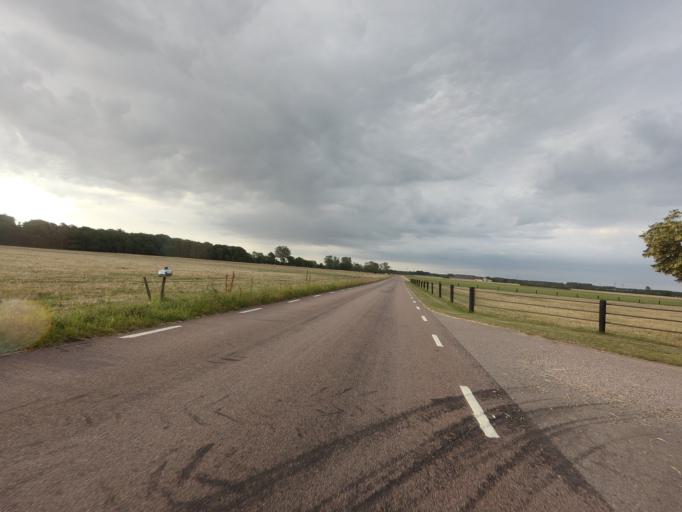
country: SE
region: Skane
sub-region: Helsingborg
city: Odakra
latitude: 56.1481
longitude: 12.7315
